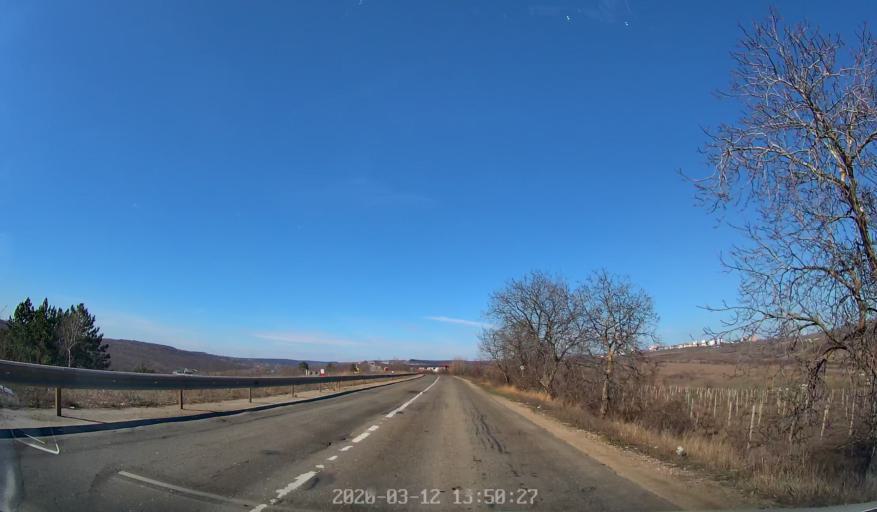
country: MD
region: Laloveni
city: Ialoveni
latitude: 46.9872
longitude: 28.7435
